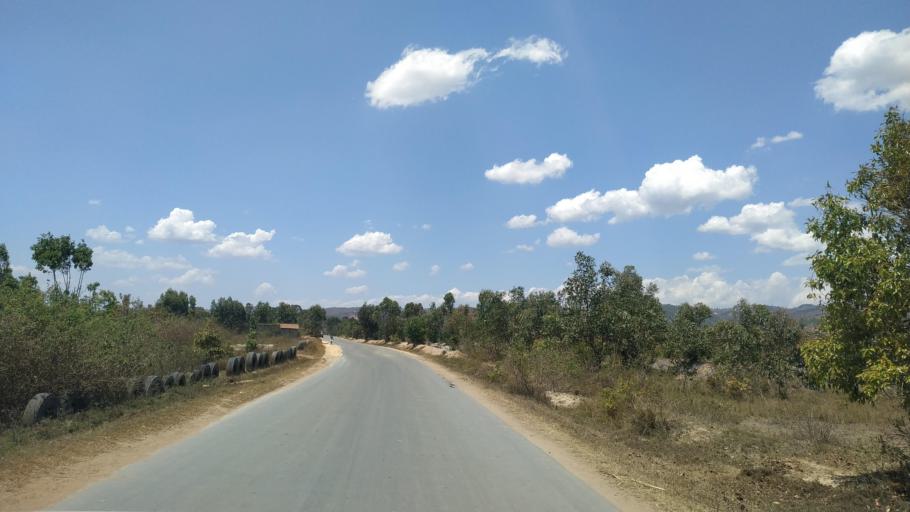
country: MG
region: Alaotra Mangoro
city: Ambatondrazaka
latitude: -18.2304
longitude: 48.2647
